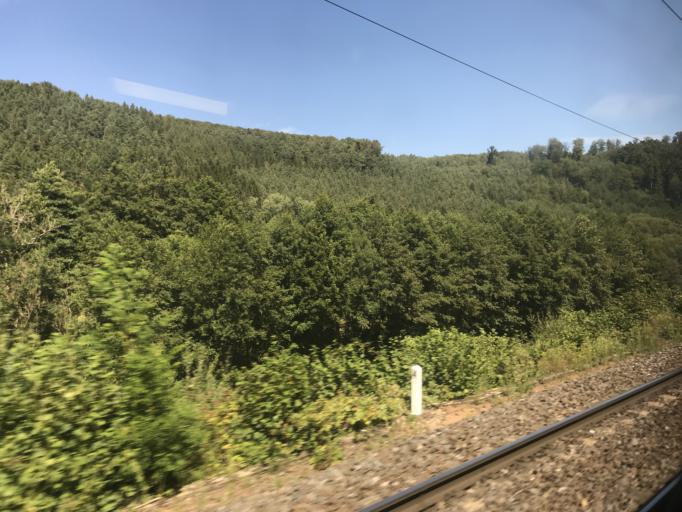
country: FR
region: Lorraine
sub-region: Departement de la Moselle
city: Phalsbourg
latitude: 48.7364
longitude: 7.2673
